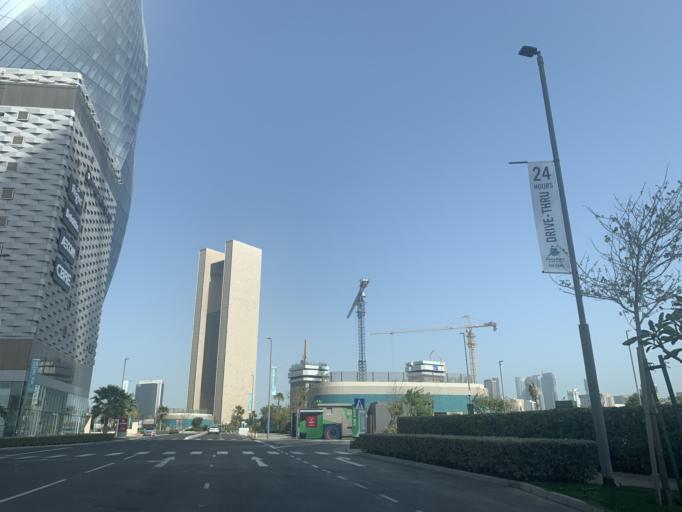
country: BH
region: Manama
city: Manama
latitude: 26.2460
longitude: 50.5764
